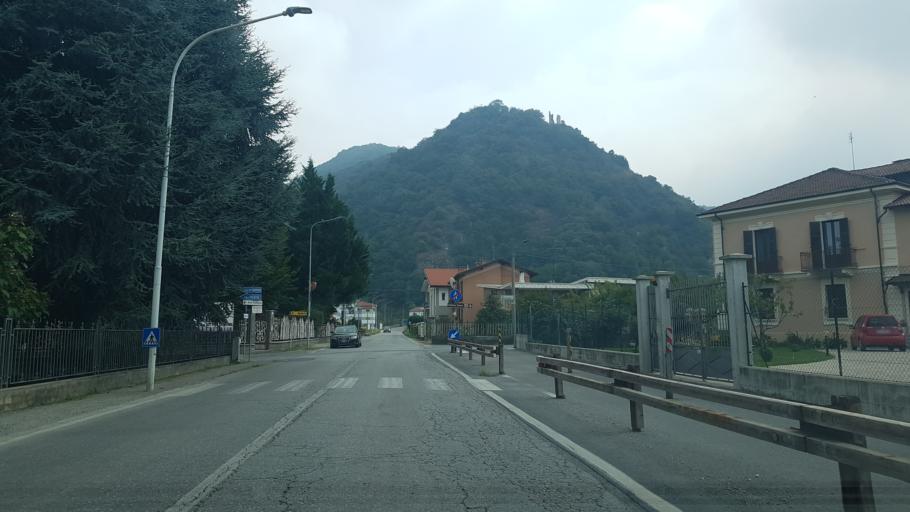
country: IT
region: Piedmont
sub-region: Provincia di Cuneo
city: Chiusa di Pesio
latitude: 44.3274
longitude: 7.6762
